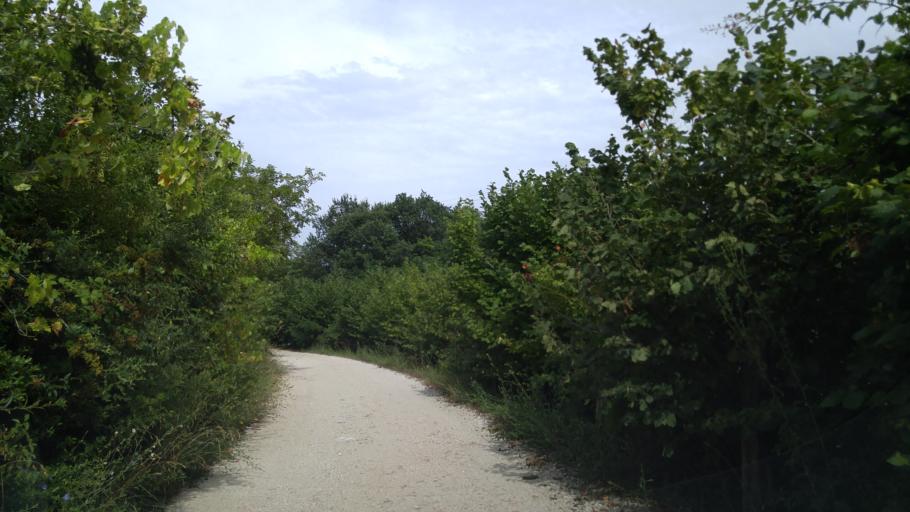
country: IT
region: The Marches
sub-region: Provincia di Pesaro e Urbino
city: Fossombrone
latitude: 43.6648
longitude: 12.7571
